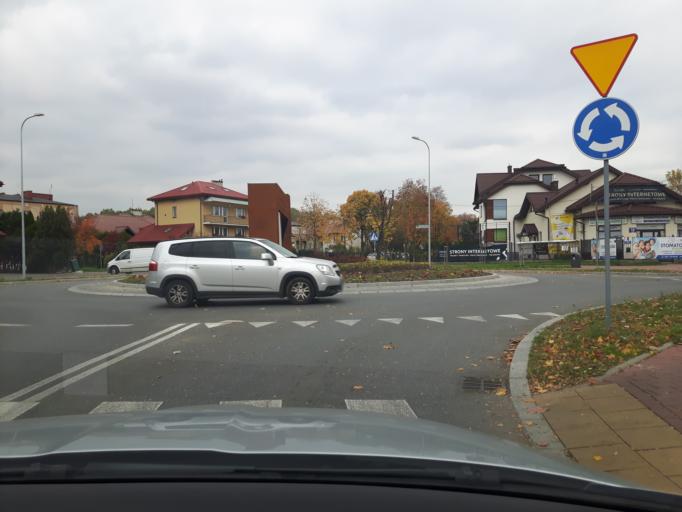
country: PL
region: Masovian Voivodeship
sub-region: Powiat wolominski
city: Zabki
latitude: 52.2953
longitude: 21.1120
